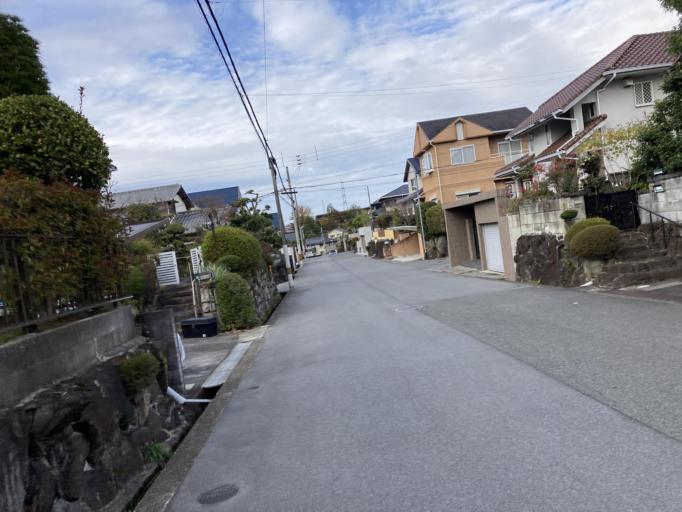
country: JP
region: Nara
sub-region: Ikoma-shi
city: Ikoma
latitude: 34.7047
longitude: 135.6999
